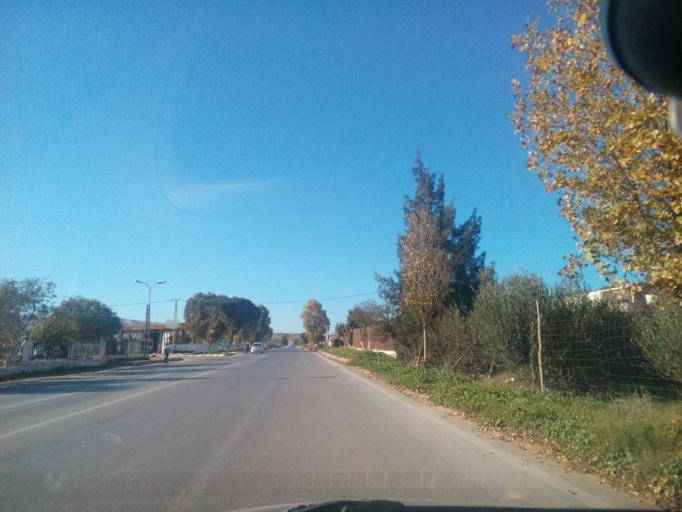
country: DZ
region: Relizane
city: Relizane
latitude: 35.9006
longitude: 0.5298
